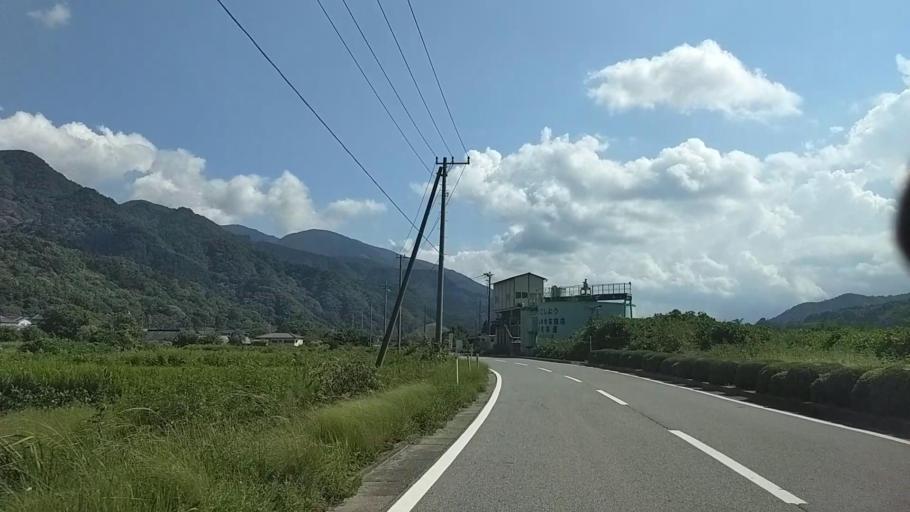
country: JP
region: Shizuoka
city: Fujinomiya
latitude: 35.3926
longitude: 138.4502
